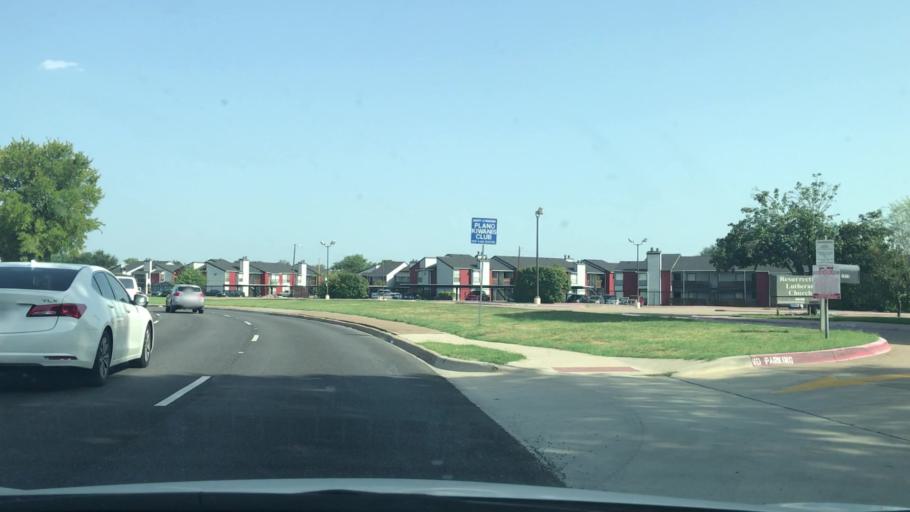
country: US
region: Texas
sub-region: Collin County
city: Plano
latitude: 33.0256
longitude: -96.7534
